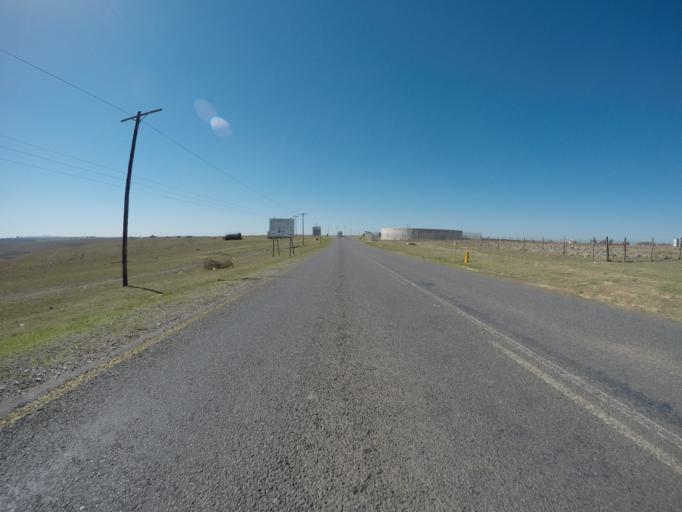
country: ZA
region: Eastern Cape
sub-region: OR Tambo District Municipality
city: Mthatha
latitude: -31.8860
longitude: 28.7608
